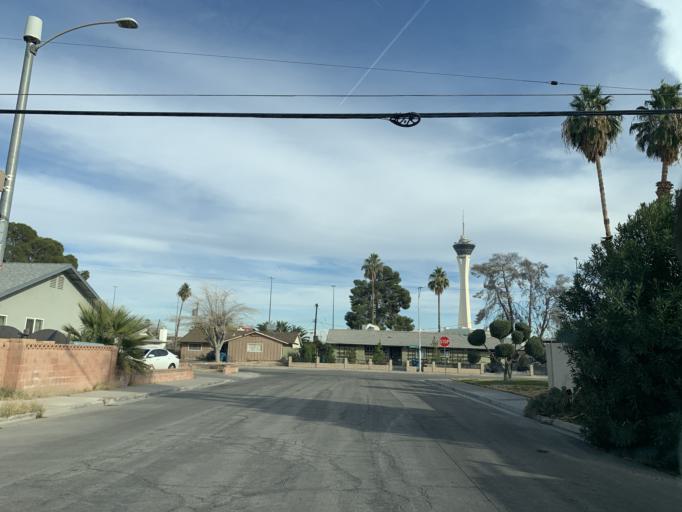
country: US
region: Nevada
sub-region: Clark County
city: Las Vegas
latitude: 36.1499
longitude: -115.1689
